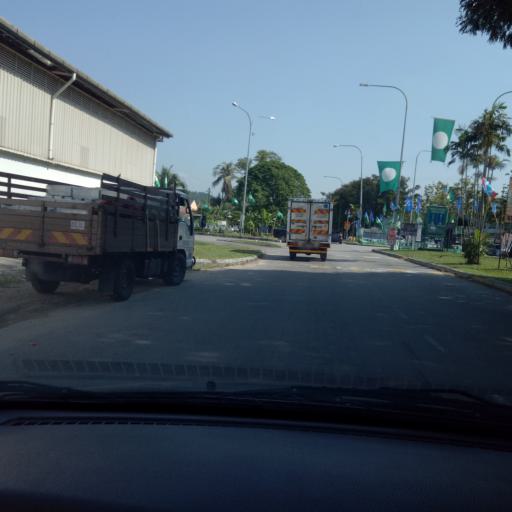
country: MY
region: Selangor
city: Kampong Baharu Balakong
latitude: 3.0255
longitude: 101.7641
